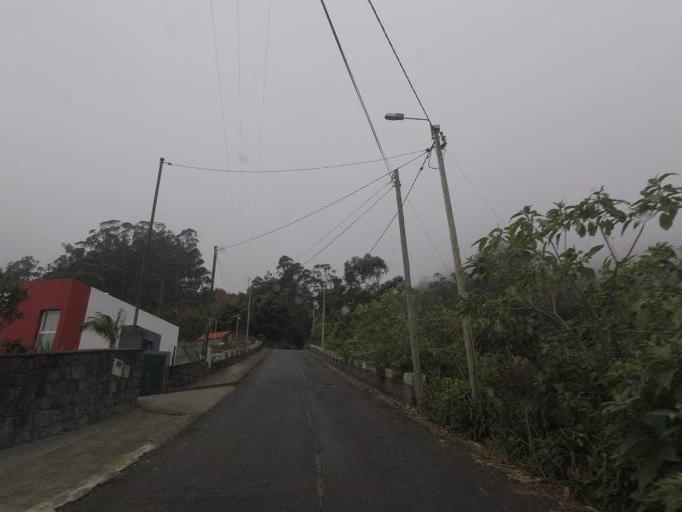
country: PT
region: Madeira
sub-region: Santa Cruz
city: Santa Cruz
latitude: 32.7324
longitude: -16.8230
